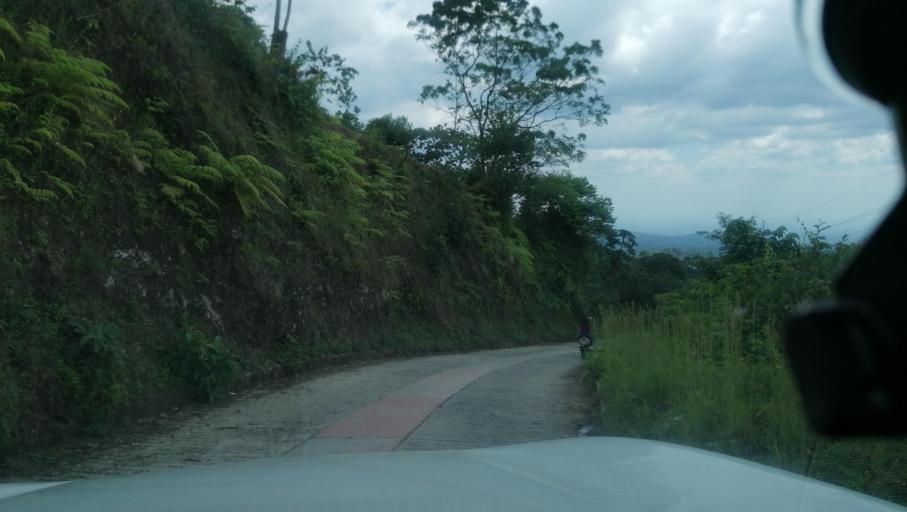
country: MX
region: Chiapas
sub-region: Cacahoatan
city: Benito Juarez
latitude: 15.0671
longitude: -92.1516
